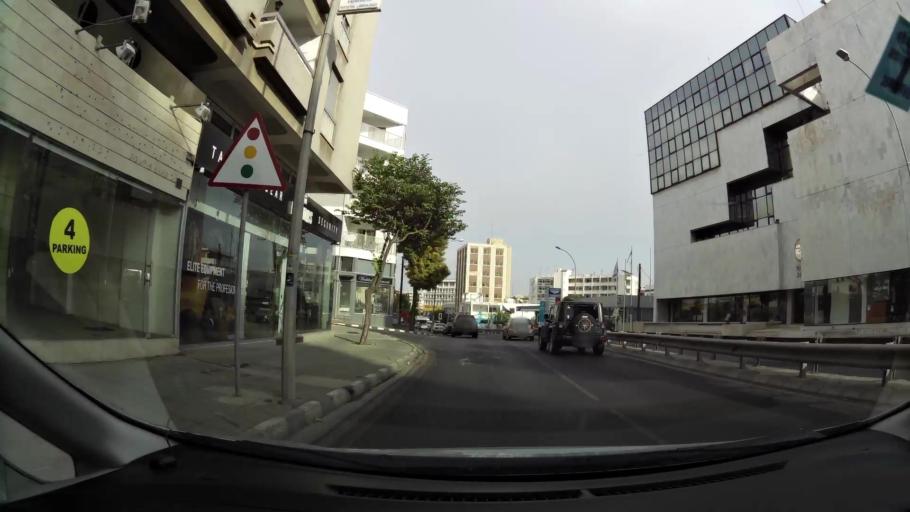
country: CY
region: Lefkosia
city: Nicosia
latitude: 35.1632
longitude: 33.3565
